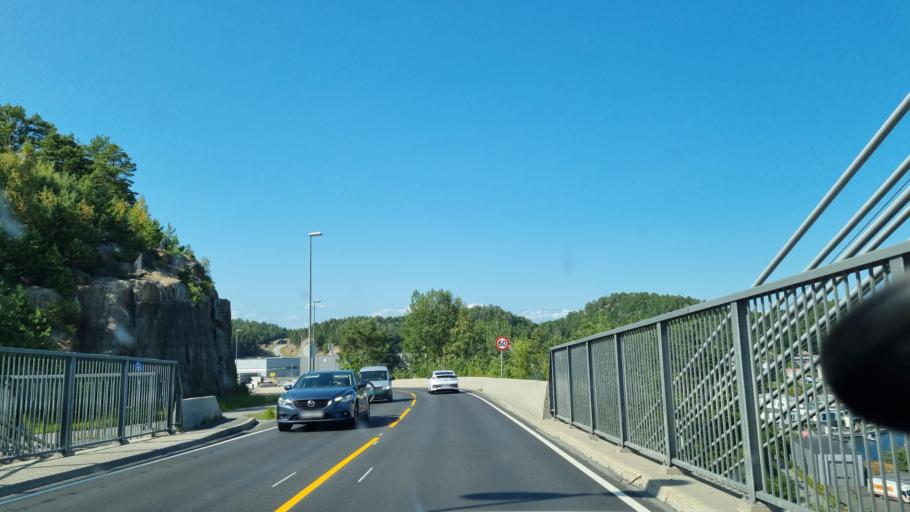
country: NO
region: Aust-Agder
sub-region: Arendal
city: Arendal
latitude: 58.4727
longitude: 8.8219
